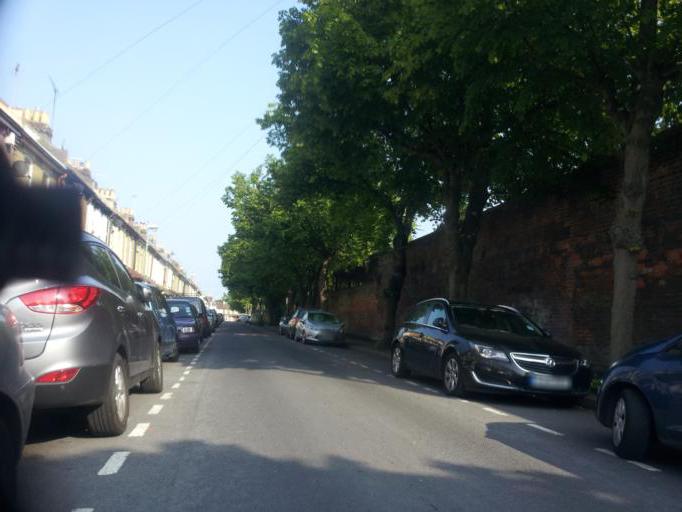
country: GB
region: England
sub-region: Kent
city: Gillingham
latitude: 51.3812
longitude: 0.5420
